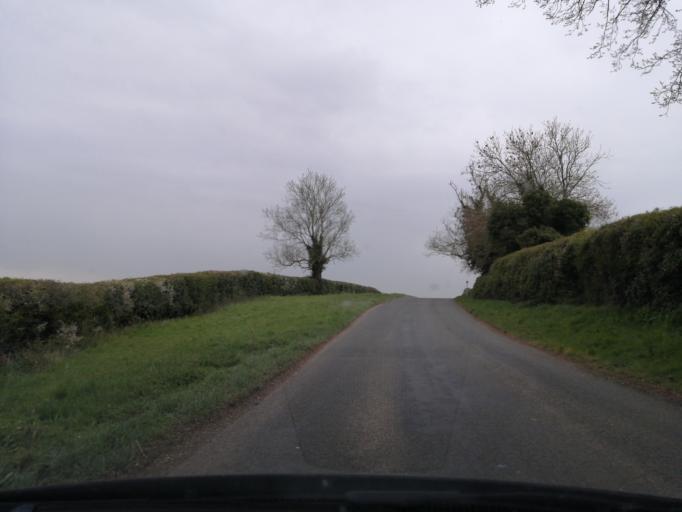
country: GB
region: England
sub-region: Peterborough
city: Wittering
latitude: 52.6095
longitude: -0.4612
